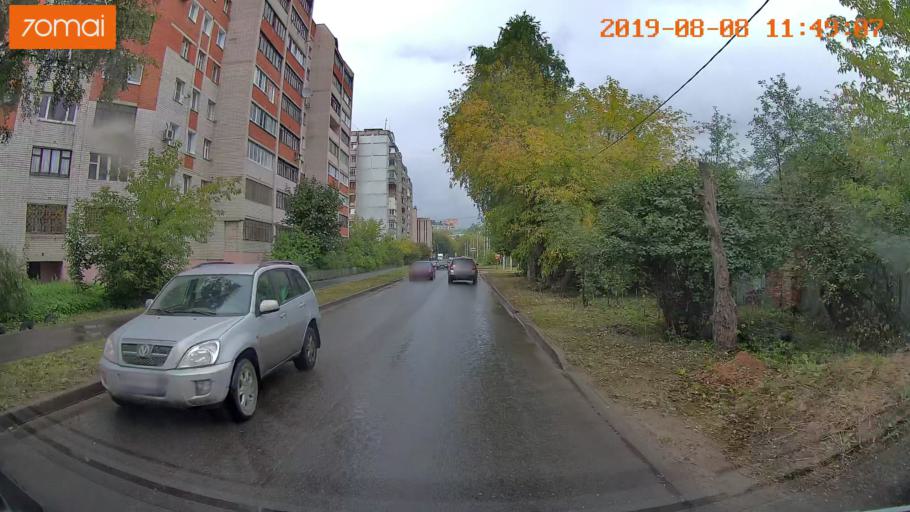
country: RU
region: Ivanovo
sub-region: Gorod Ivanovo
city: Ivanovo
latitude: 56.9756
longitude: 40.9833
